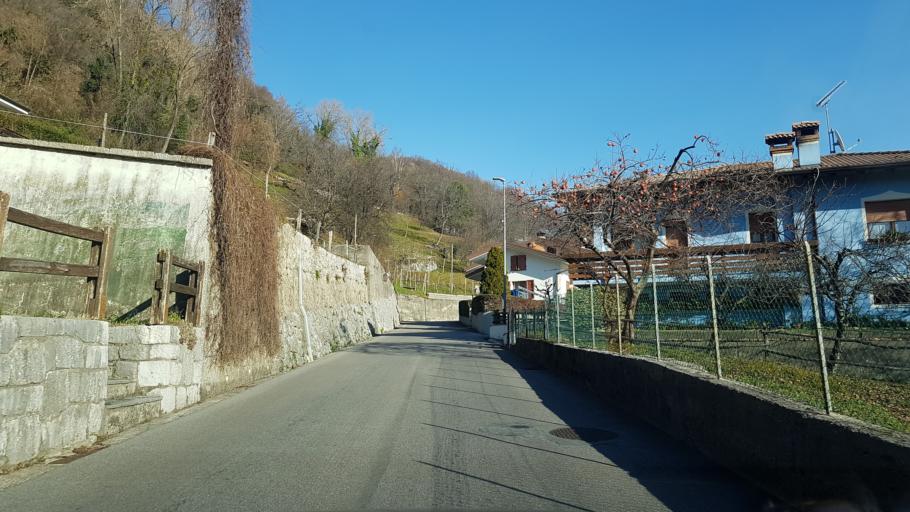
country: IT
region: Friuli Venezia Giulia
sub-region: Provincia di Udine
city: Forgaria nel Friuli
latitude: 46.2253
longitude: 12.9711
